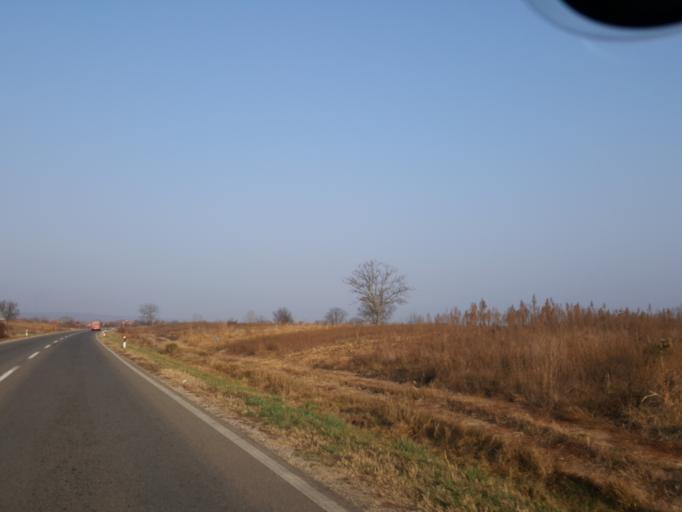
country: RS
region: Central Serbia
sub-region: Jablanicki Okrug
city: Leskovac
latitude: 42.9193
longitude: 22.0253
